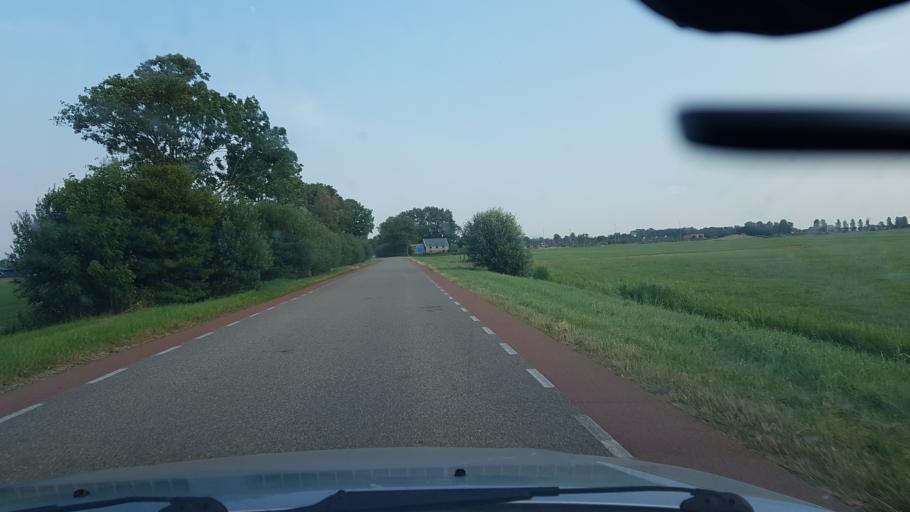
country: NL
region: Friesland
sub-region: Gemeente Ferwerderadiel
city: Burdaard
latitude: 53.3028
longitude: 5.8741
